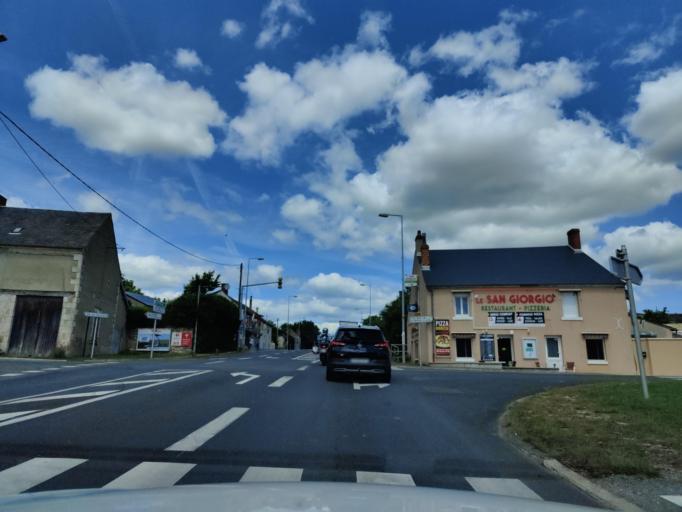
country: FR
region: Centre
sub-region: Departement du Cher
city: Fussy
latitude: 47.1897
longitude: 2.4234
